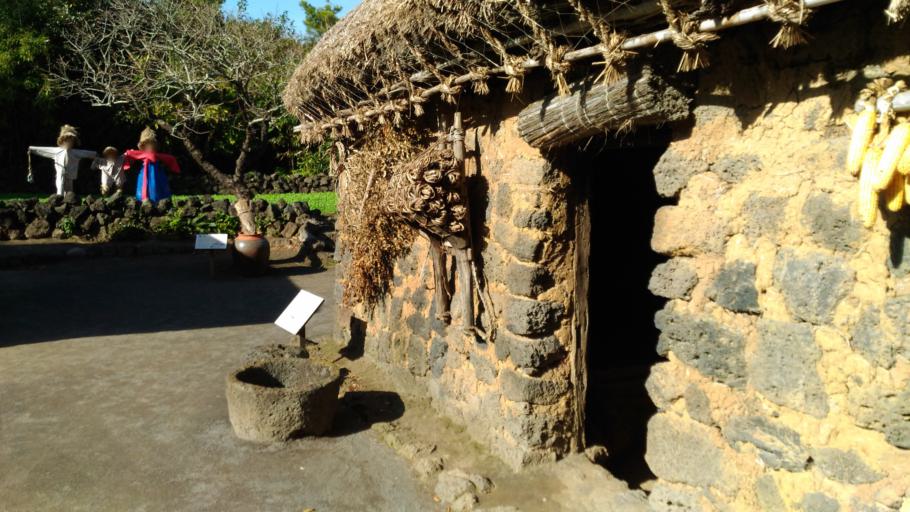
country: KR
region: Jeju-do
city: Seogwipo
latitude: 33.3235
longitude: 126.8403
